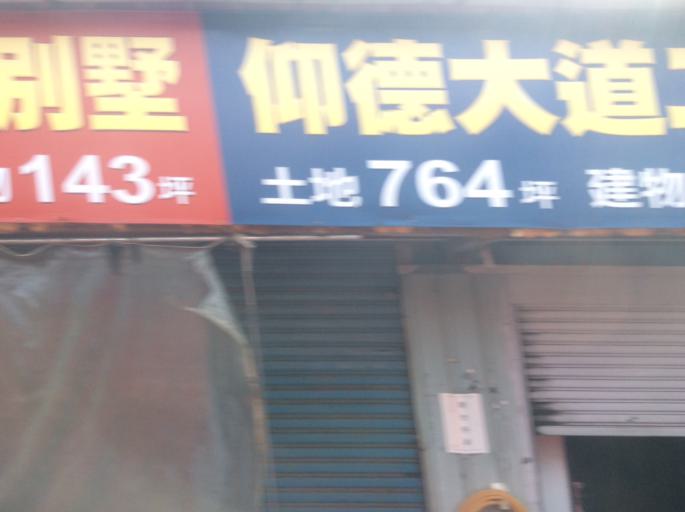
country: TW
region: Taipei
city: Taipei
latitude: 25.1426
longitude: 121.5494
